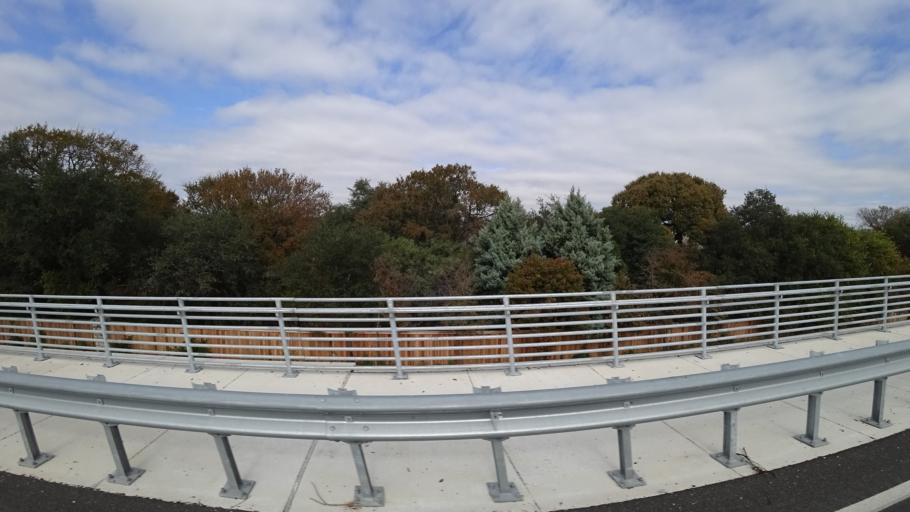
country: US
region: Texas
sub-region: Williamson County
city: Round Rock
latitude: 30.5345
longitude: -97.7005
